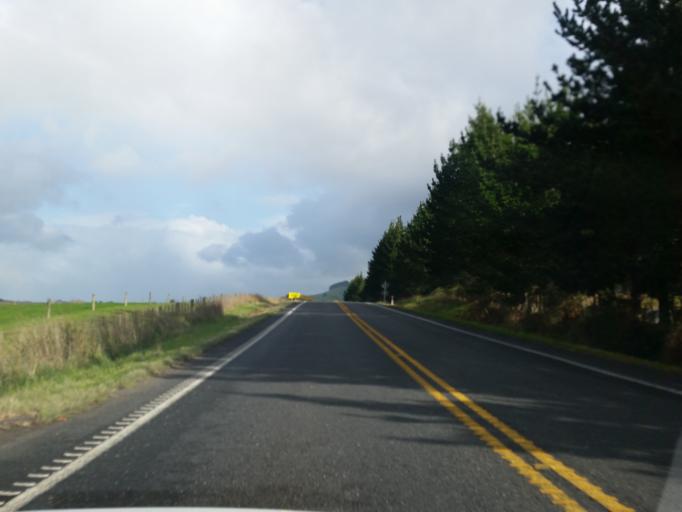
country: NZ
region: Auckland
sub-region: Auckland
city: Pukekohe East
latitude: -37.2145
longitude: 175.0678
